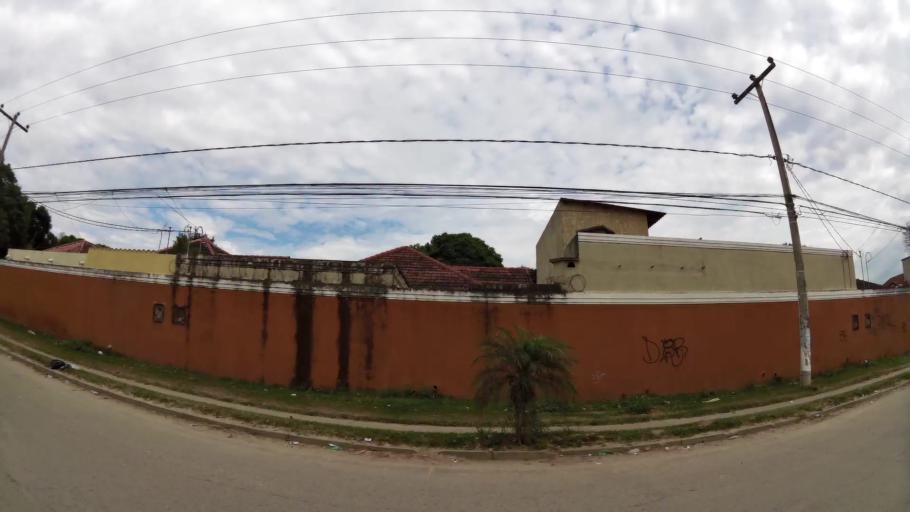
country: BO
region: Santa Cruz
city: Santa Cruz de la Sierra
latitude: -17.7451
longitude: -63.1886
